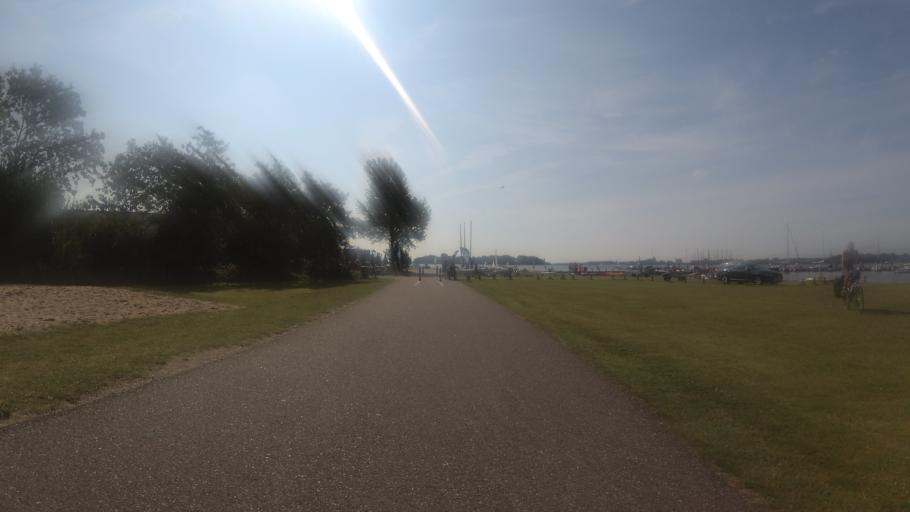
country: NL
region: Zeeland
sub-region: Gemeente Veere
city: Veere
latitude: 51.5686
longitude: 3.6610
